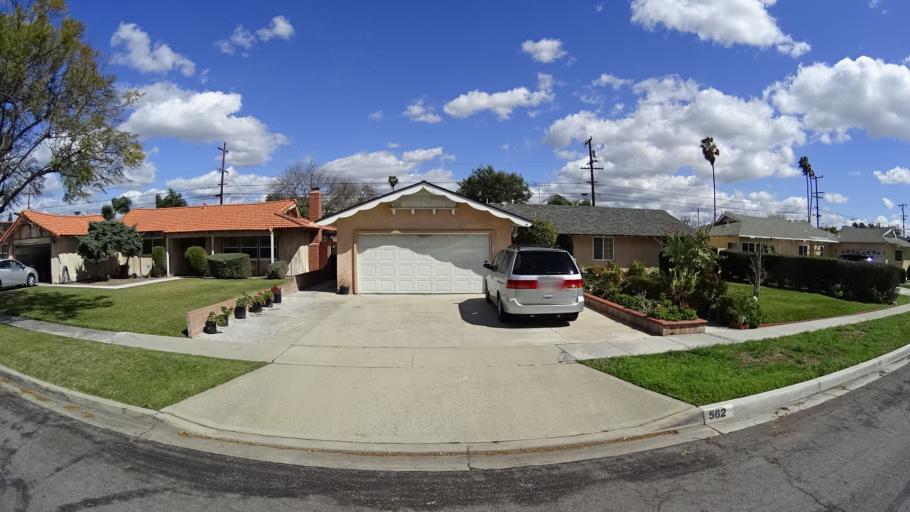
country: US
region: California
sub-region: Orange County
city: Anaheim
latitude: 33.8331
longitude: -117.8941
